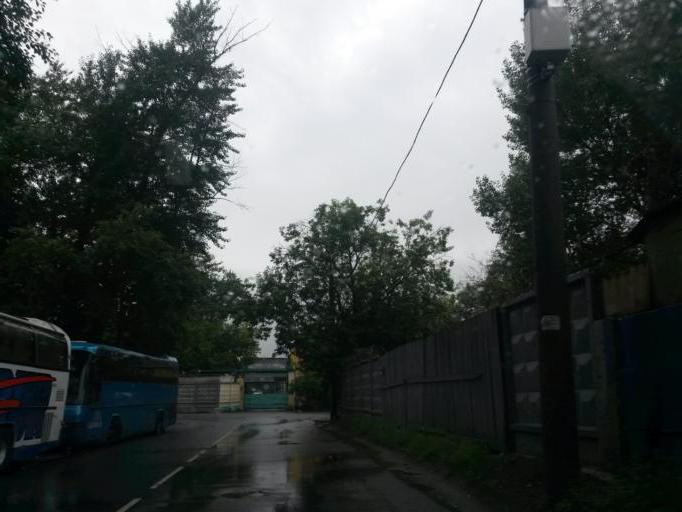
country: RU
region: Moscow
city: Zamoskvorech'ye
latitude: 55.7095
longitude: 37.6339
